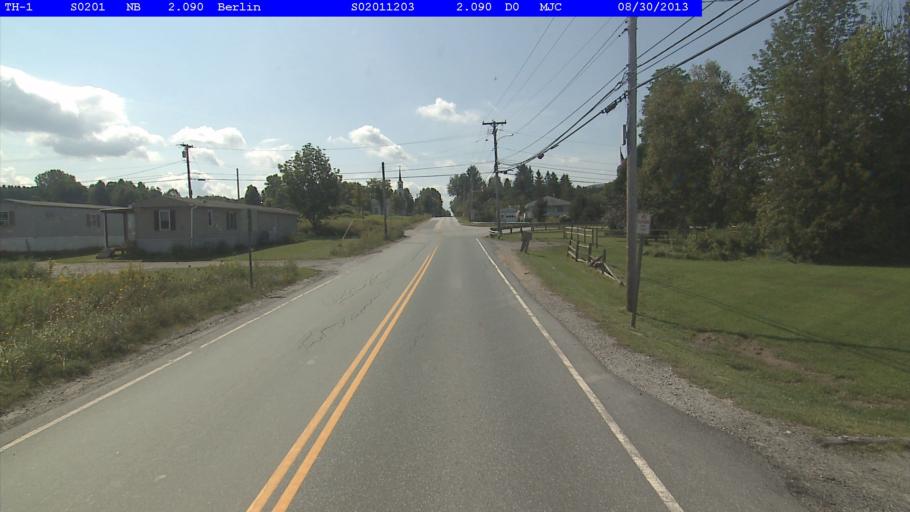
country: US
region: Vermont
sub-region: Washington County
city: Montpelier
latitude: 44.2106
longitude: -72.5761
